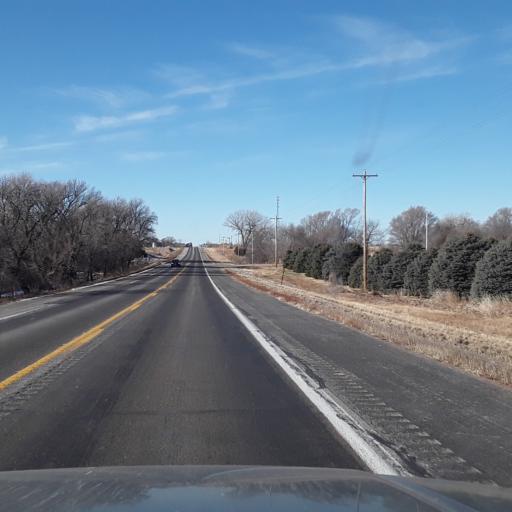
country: US
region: Nebraska
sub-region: Adams County
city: Hastings
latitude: 40.5681
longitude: -98.4948
